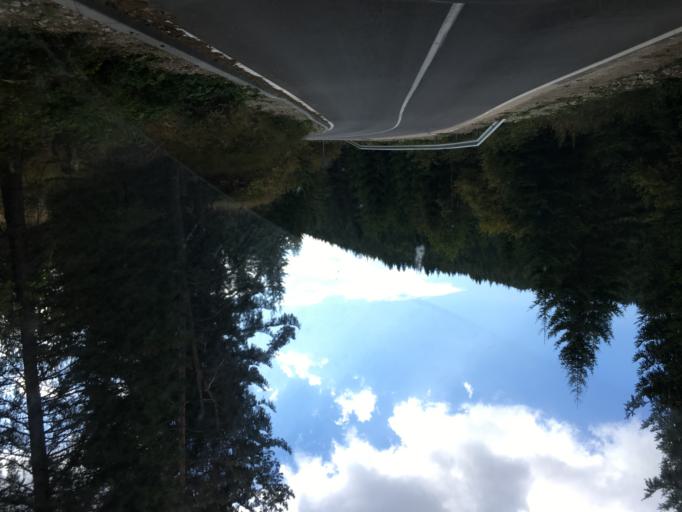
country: BG
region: Pazardzhik
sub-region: Obshtina Batak
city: Batak
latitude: 41.9041
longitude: 24.3003
